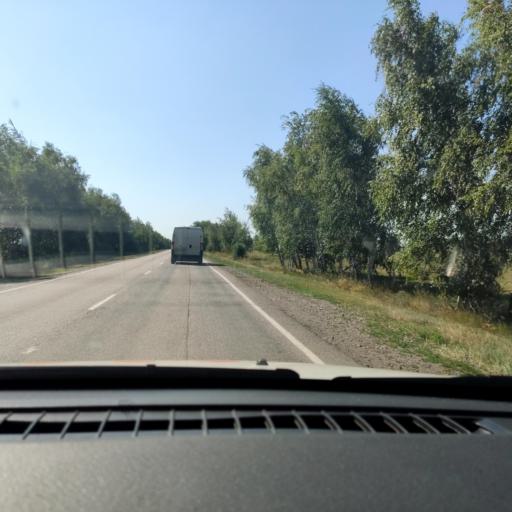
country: RU
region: Voronezj
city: Liski
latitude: 50.8016
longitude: 39.3324
